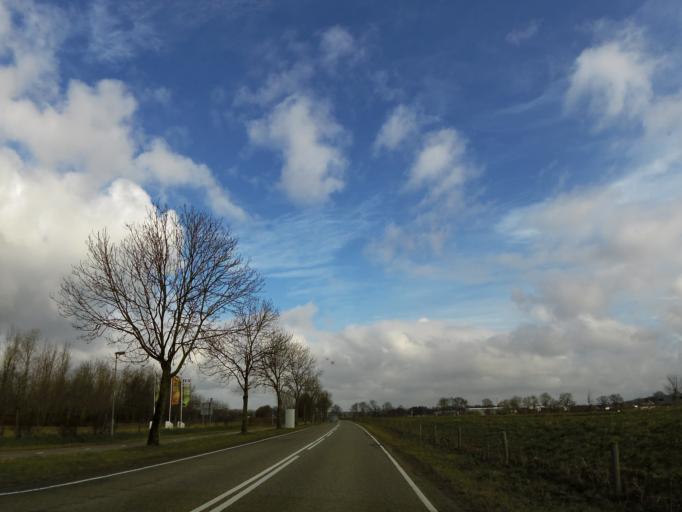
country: NL
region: Limburg
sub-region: Eijsden-Margraten
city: Eijsden
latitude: 50.8067
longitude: 5.7090
